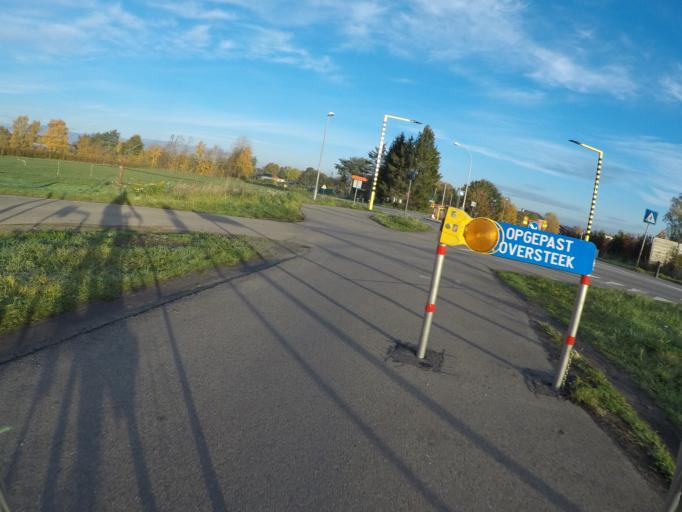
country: BE
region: Flanders
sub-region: Provincie Antwerpen
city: Herentals
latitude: 51.1513
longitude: 4.8208
